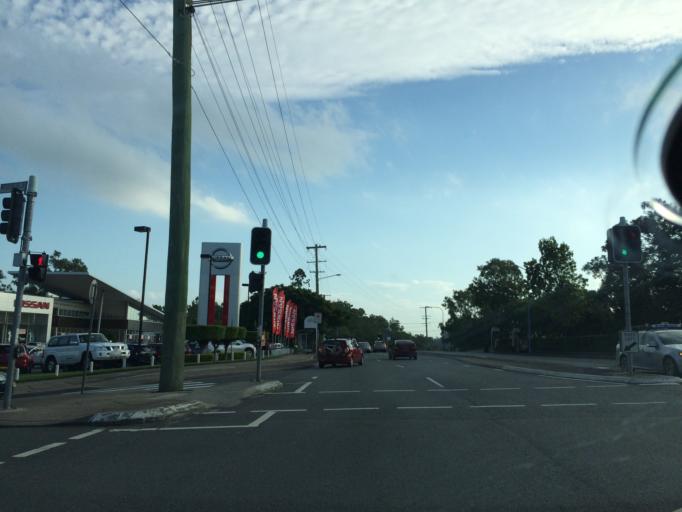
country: AU
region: Queensland
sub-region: Brisbane
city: Taringa
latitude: -27.4998
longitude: 152.9674
